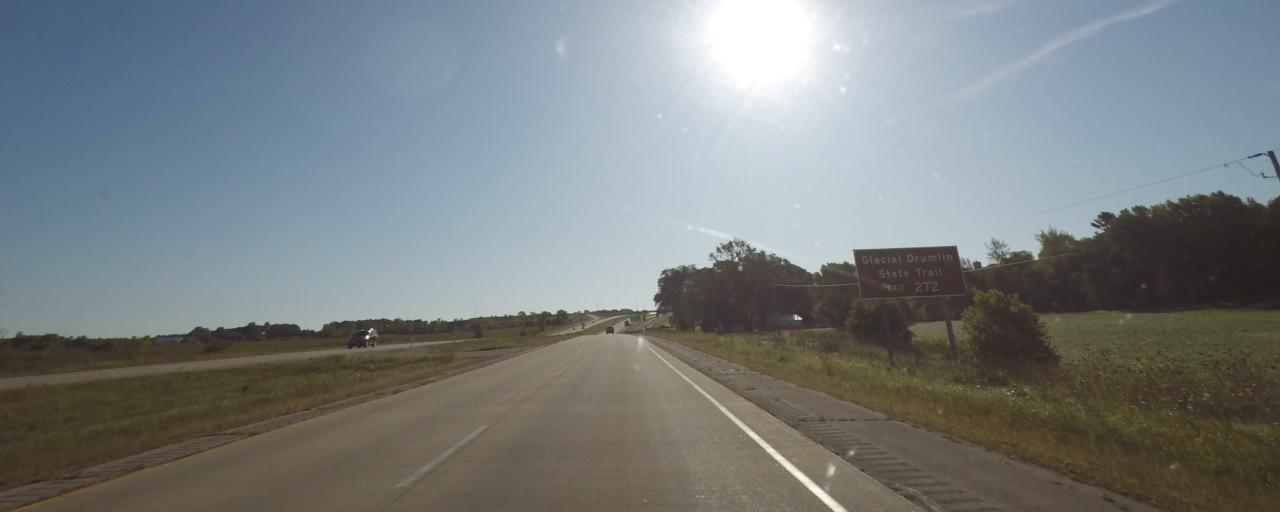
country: US
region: Wisconsin
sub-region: Dane County
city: Cottage Grove
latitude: 43.0331
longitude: -89.2126
